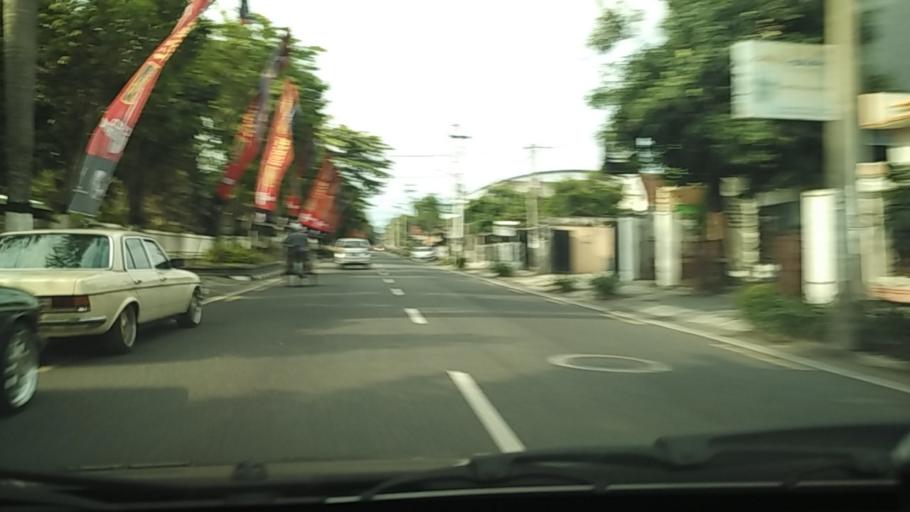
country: ID
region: Daerah Istimewa Yogyakarta
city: Yogyakarta
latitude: -7.8007
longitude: 110.3844
